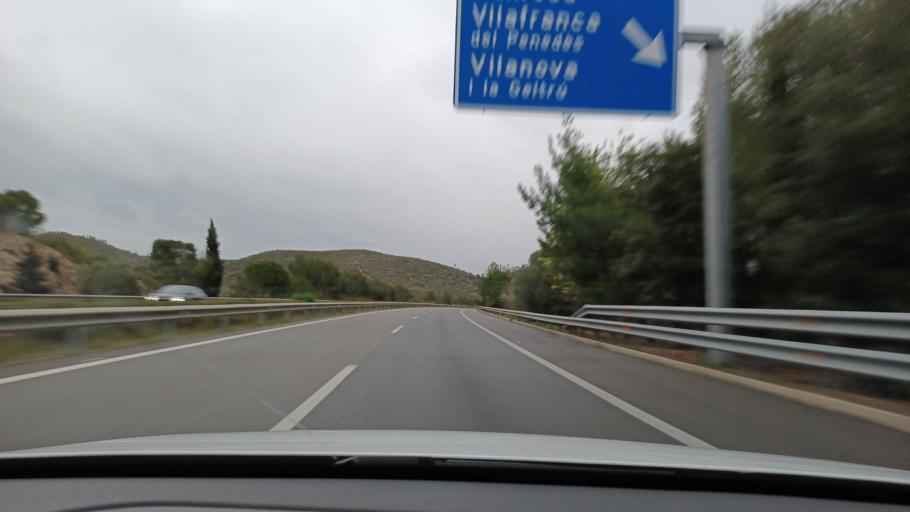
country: ES
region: Catalonia
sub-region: Provincia de Barcelona
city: Vilanova i la Geltru
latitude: 41.2496
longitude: 1.6992
